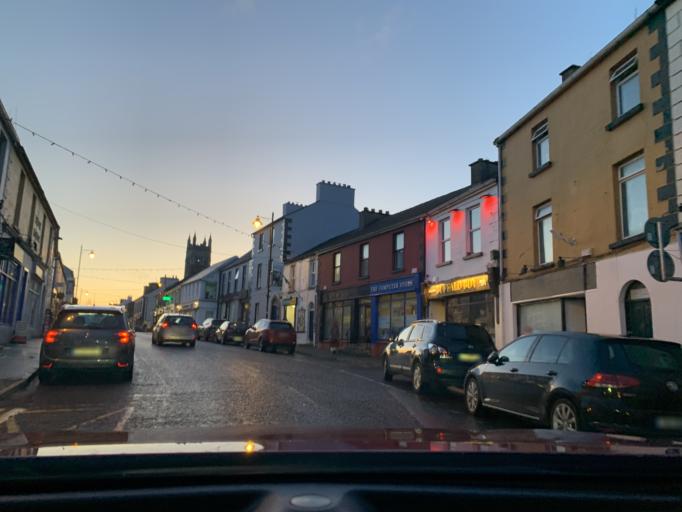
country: IE
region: Connaught
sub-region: County Leitrim
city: Carrick-on-Shannon
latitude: 53.9469
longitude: -8.0927
